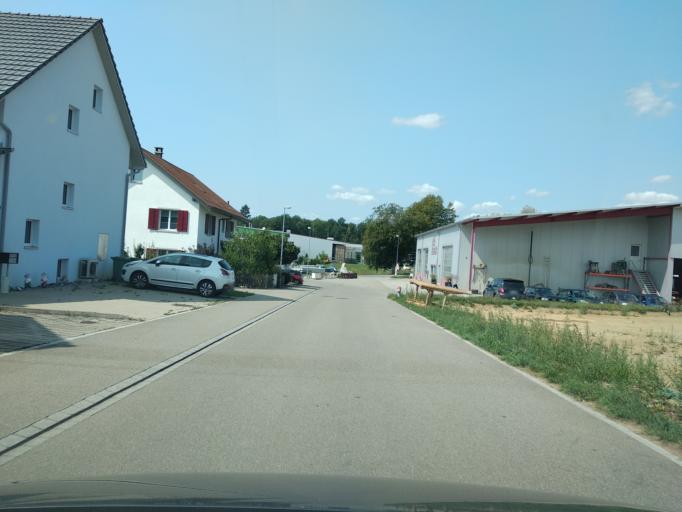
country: CH
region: Zurich
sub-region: Bezirk Andelfingen
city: Marthalen
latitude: 47.6345
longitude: 8.6521
